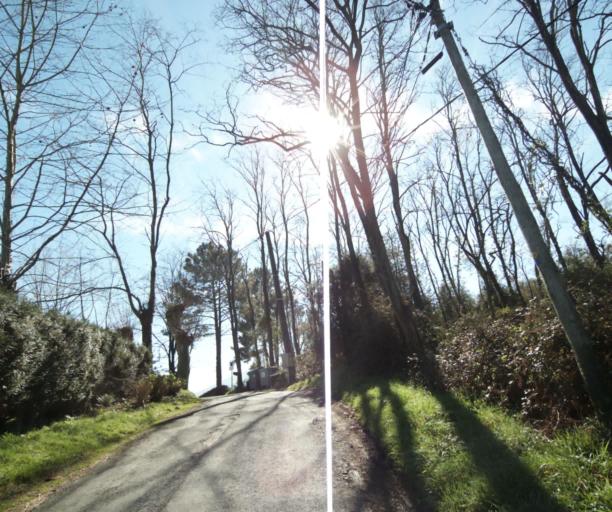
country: FR
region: Aquitaine
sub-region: Departement des Pyrenees-Atlantiques
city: Ascain
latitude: 43.3531
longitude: -1.6550
